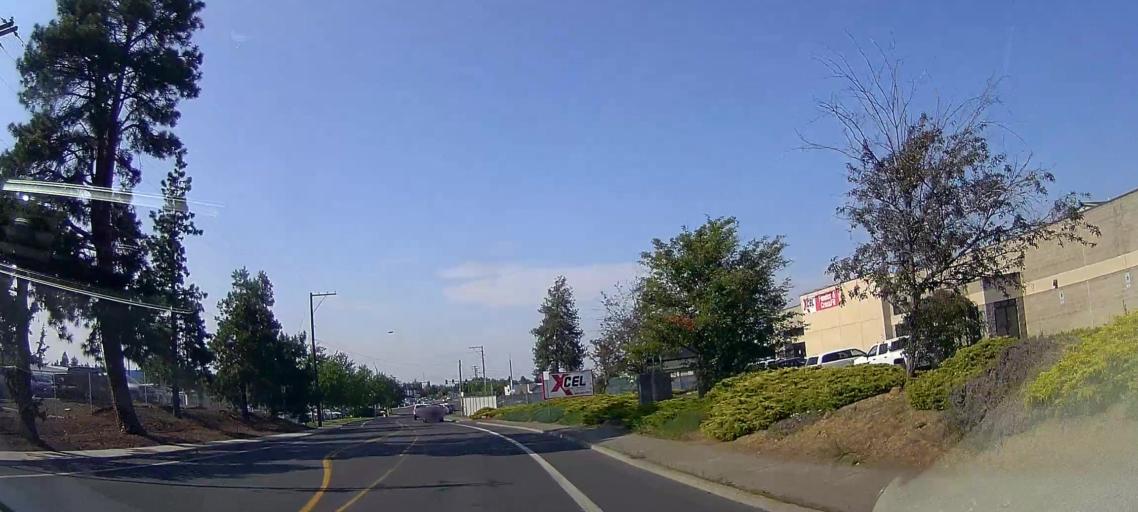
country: US
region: Oregon
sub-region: Deschutes County
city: Bend
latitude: 44.0536
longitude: -121.2686
